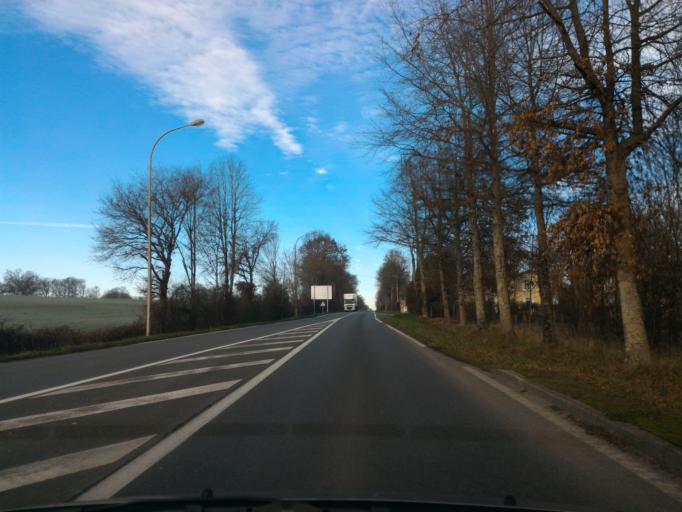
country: FR
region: Poitou-Charentes
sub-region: Departement de la Charente
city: Confolens
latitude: 46.0246
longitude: 0.6523
